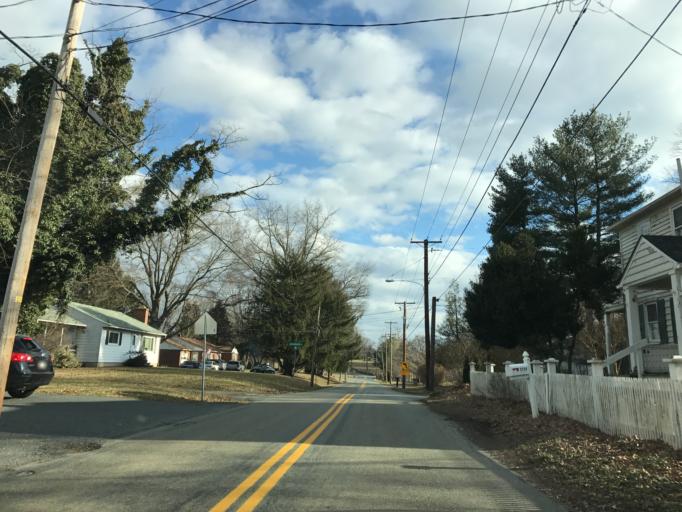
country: US
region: Maryland
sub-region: Harford County
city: Aberdeen
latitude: 39.6364
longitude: -76.1987
